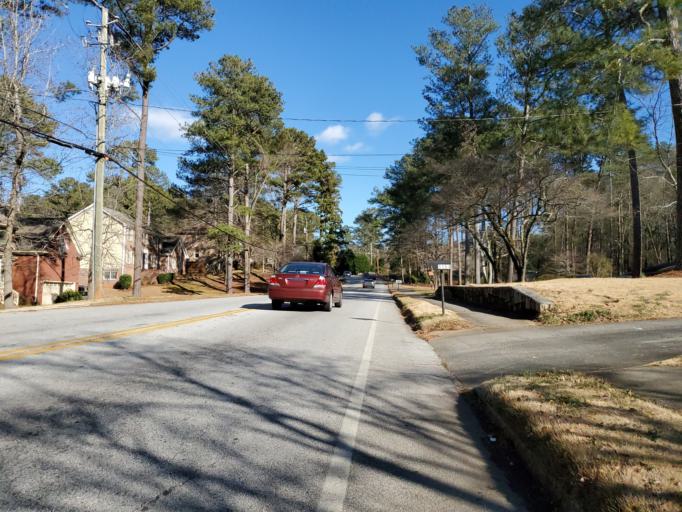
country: US
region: Georgia
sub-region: DeKalb County
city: Clarkston
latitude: 33.7683
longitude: -84.2200
